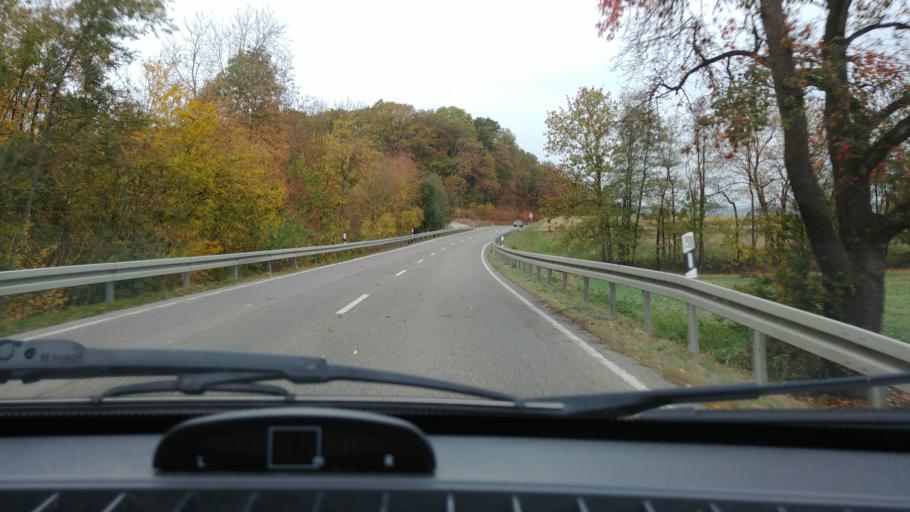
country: DE
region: Baden-Wuerttemberg
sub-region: Regierungsbezirk Stuttgart
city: Wallhausen
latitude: 49.2187
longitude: 10.0581
